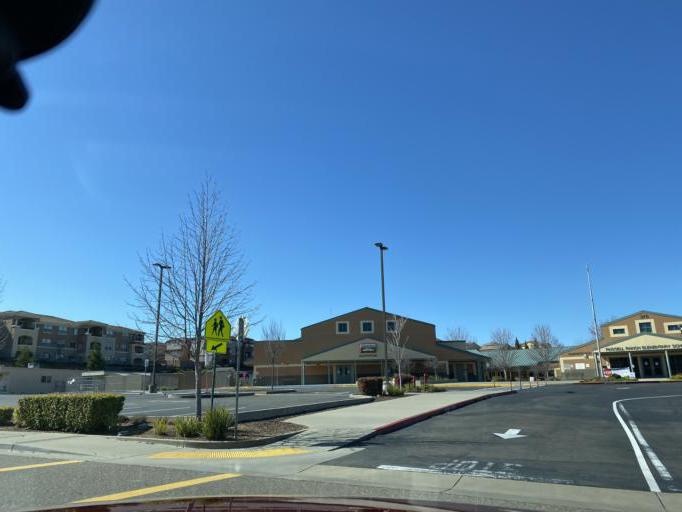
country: US
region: California
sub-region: El Dorado County
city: El Dorado Hills
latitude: 38.6515
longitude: -121.0892
